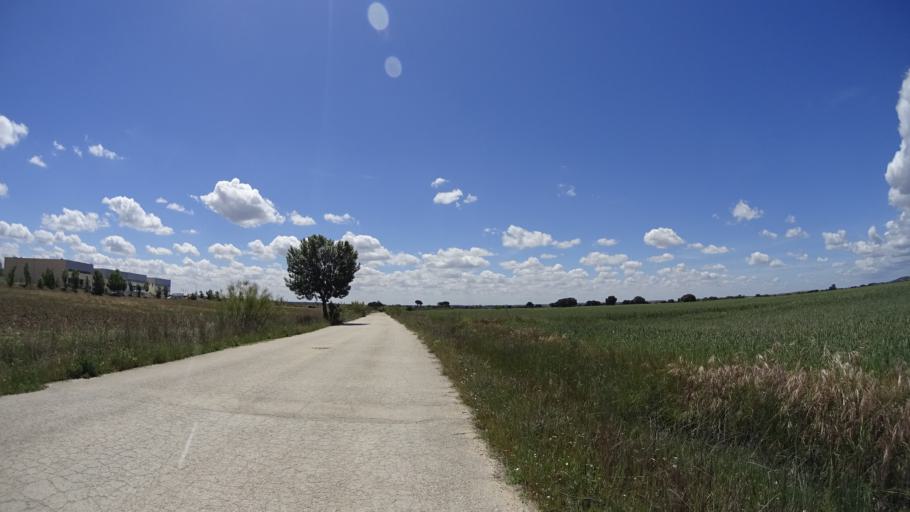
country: ES
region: Madrid
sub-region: Provincia de Madrid
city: Villanueva del Pardillo
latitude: 40.4911
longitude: -3.9886
